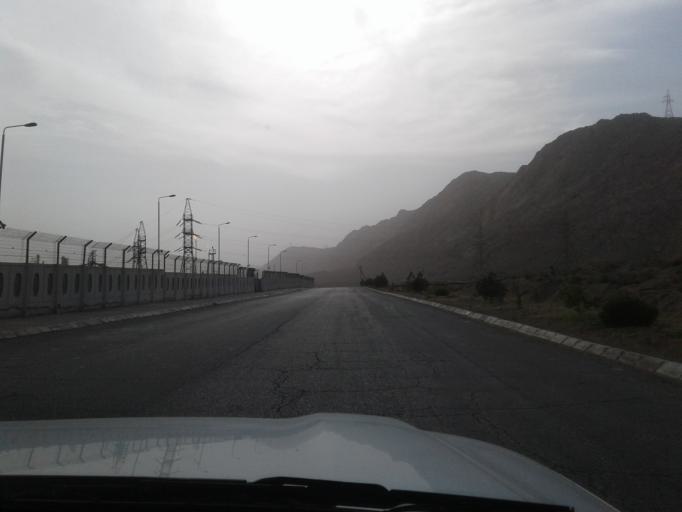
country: TM
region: Balkan
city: Turkmenbasy
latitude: 40.0339
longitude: 52.9610
